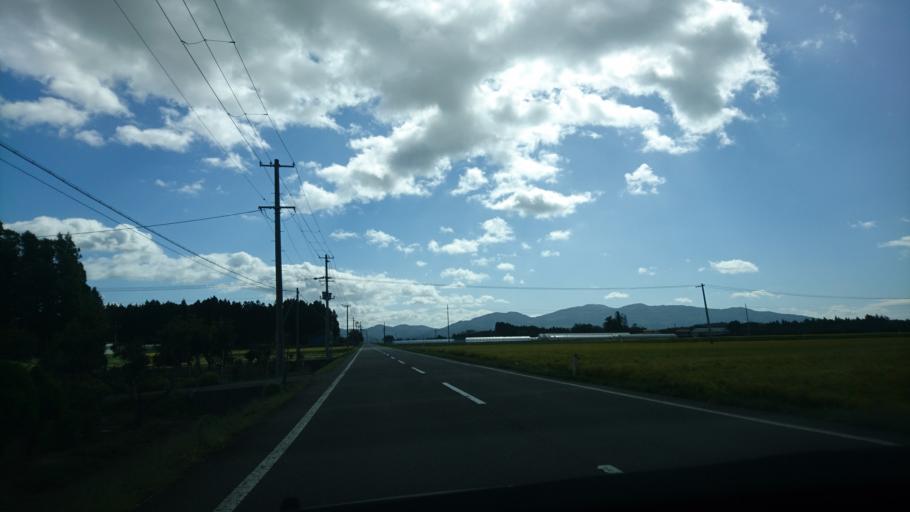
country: JP
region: Iwate
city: Mizusawa
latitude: 39.0768
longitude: 141.1084
